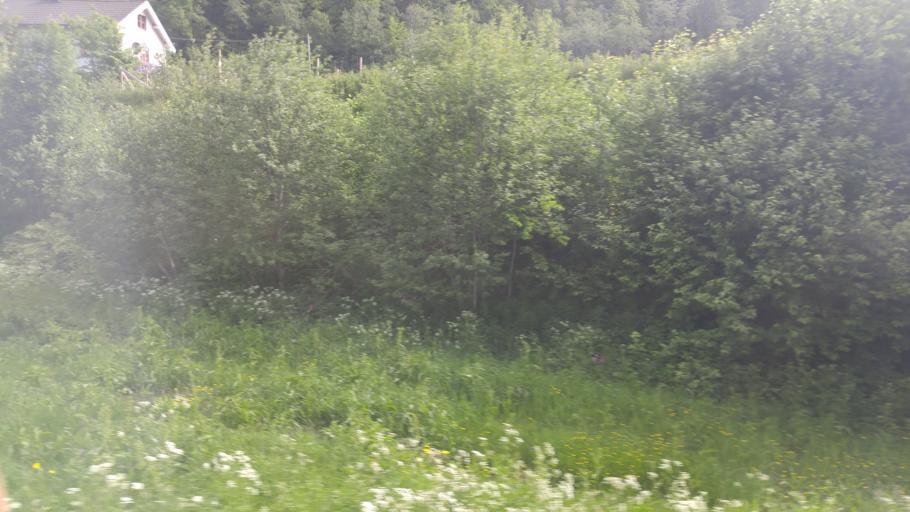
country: NO
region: Sor-Trondelag
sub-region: Midtre Gauldal
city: Storen
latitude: 63.0036
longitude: 10.4598
